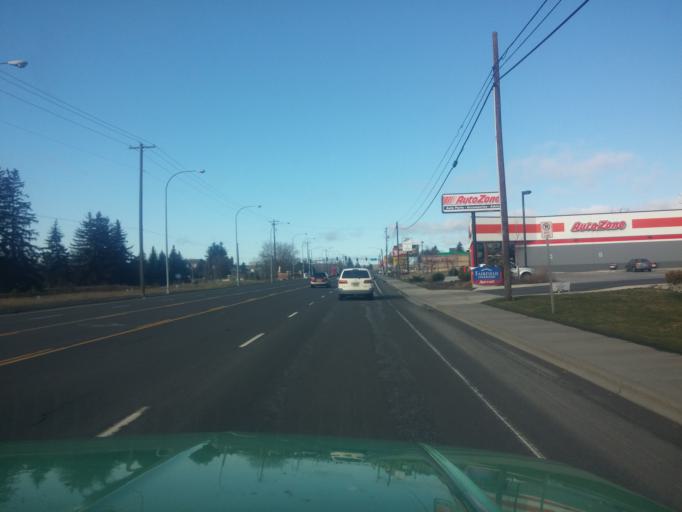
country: US
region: Idaho
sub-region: Latah County
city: Moscow
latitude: 46.7333
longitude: -117.0134
